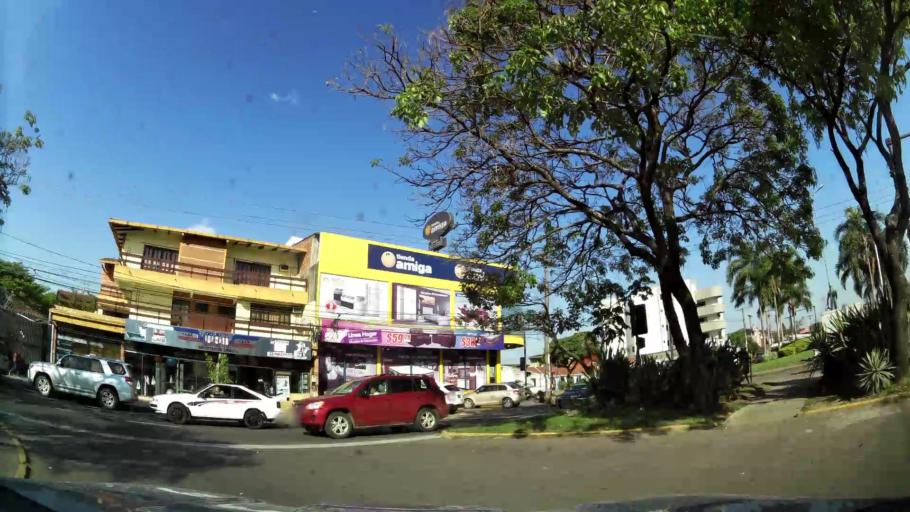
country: BO
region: Santa Cruz
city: Santa Cruz de la Sierra
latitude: -17.7851
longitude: -63.1719
